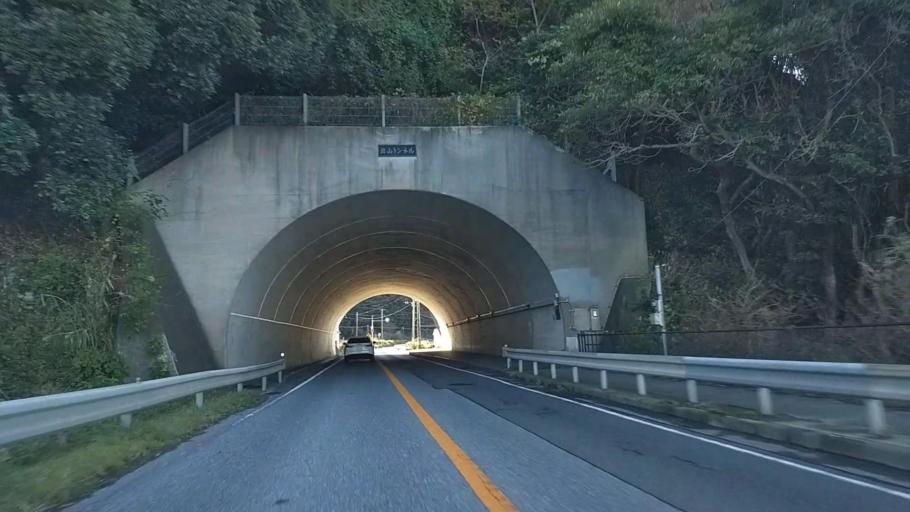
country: JP
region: Chiba
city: Futtsu
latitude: 35.1810
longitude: 139.8194
